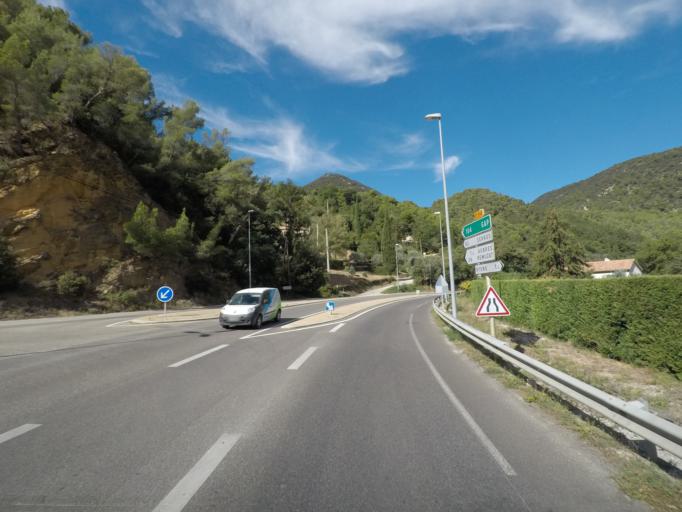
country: FR
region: Rhone-Alpes
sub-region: Departement de la Drome
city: Nyons
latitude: 44.3670
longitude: 5.1513
